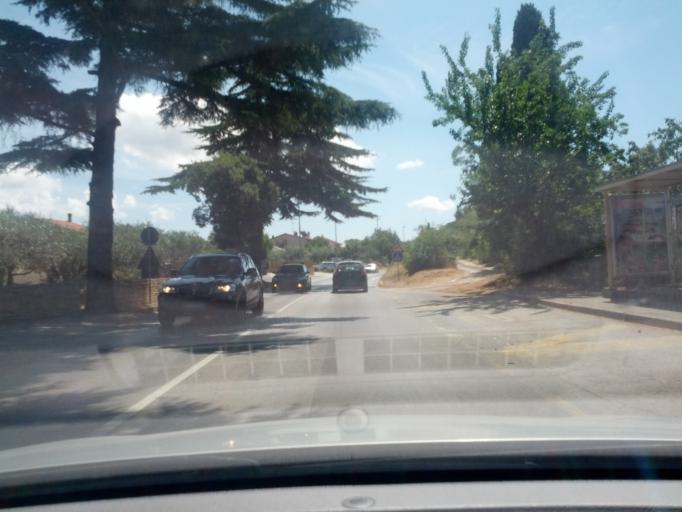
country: HR
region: Istarska
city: Fazana
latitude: 44.9141
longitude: 13.8175
